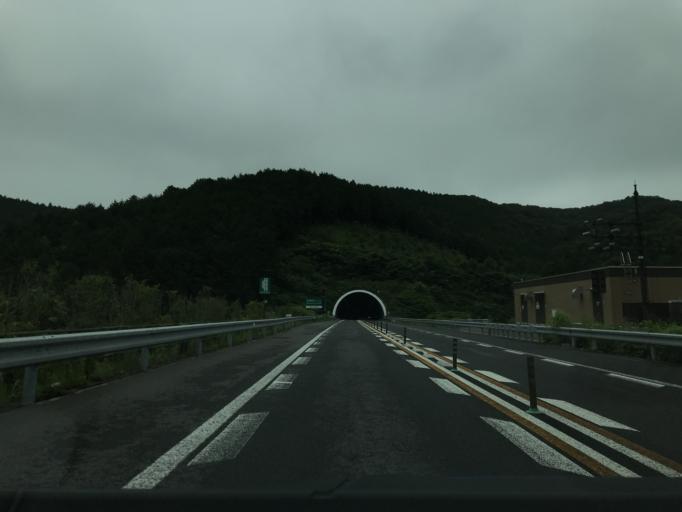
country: JP
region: Fukuoka
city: Nakatsu
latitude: 33.5123
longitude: 131.2834
